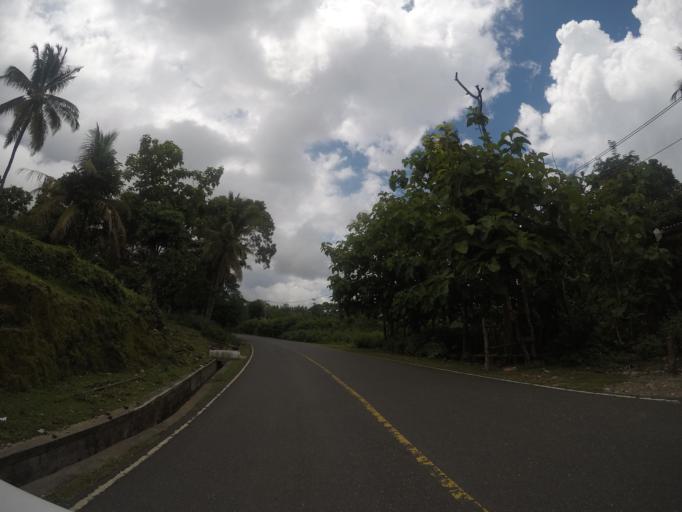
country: TL
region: Bobonaro
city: Maliana
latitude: -8.9670
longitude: 125.0507
